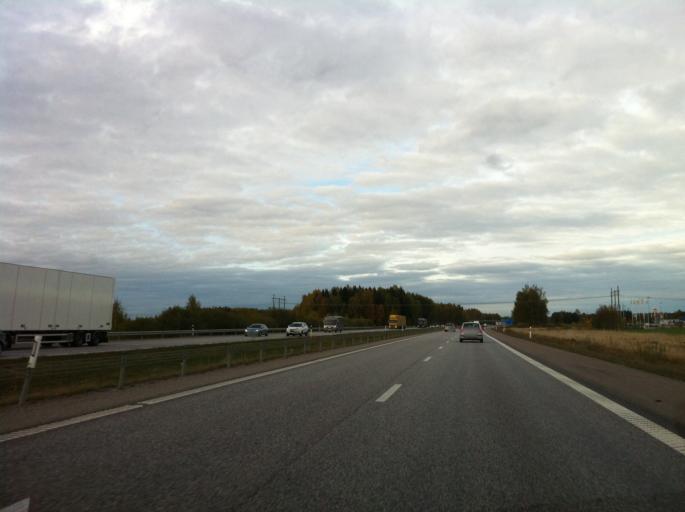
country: SE
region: OErebro
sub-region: Kumla Kommun
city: Kumla
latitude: 59.1978
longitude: 15.1261
